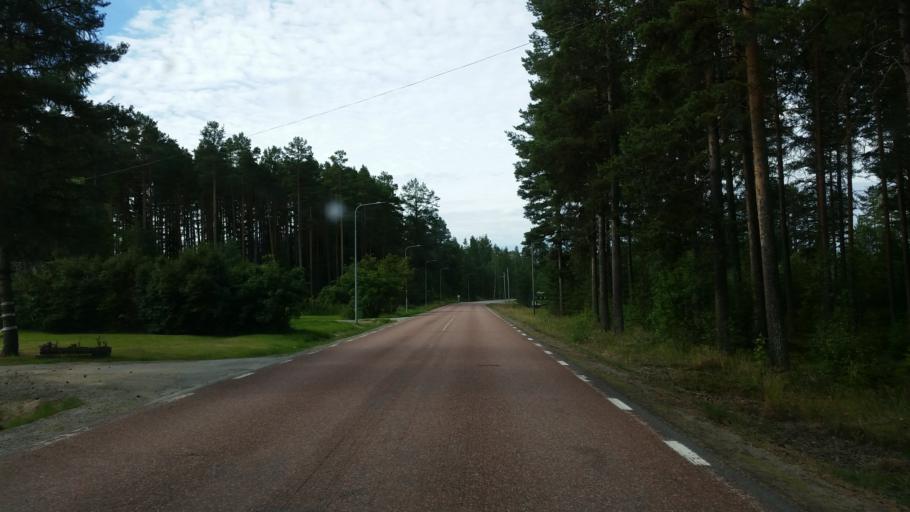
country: SE
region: Vaesternorrland
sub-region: Ange Kommun
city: Ange
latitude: 62.1900
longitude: 15.6604
